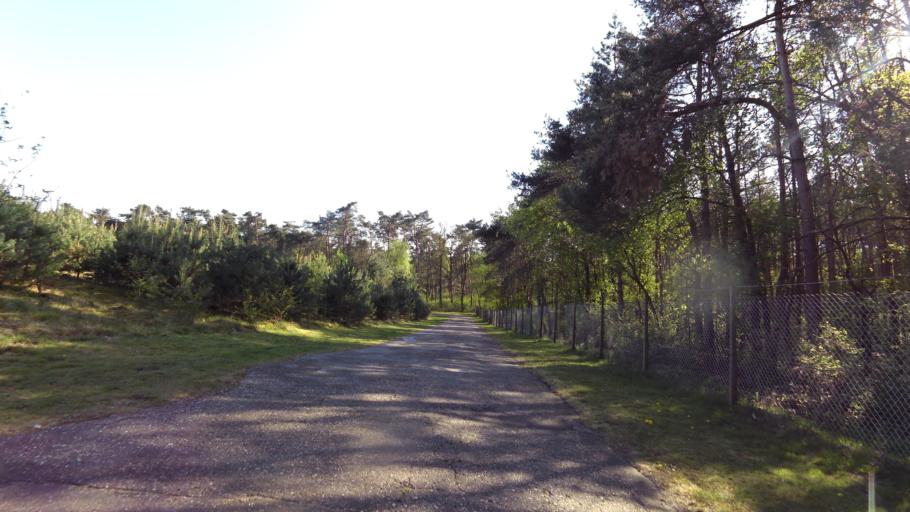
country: NL
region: Gelderland
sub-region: Gemeente Renkum
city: Wolfheze
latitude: 52.0041
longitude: 5.8131
